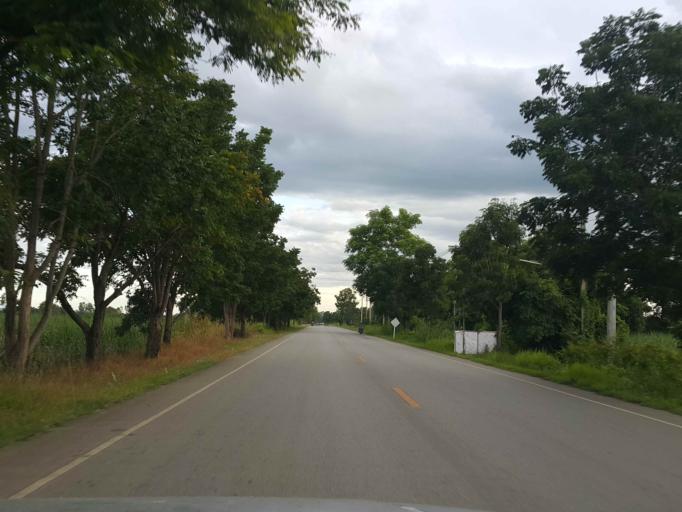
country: TH
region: Sukhothai
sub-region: Amphoe Si Satchanalai
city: Si Satchanalai
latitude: 17.4781
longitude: 99.7410
